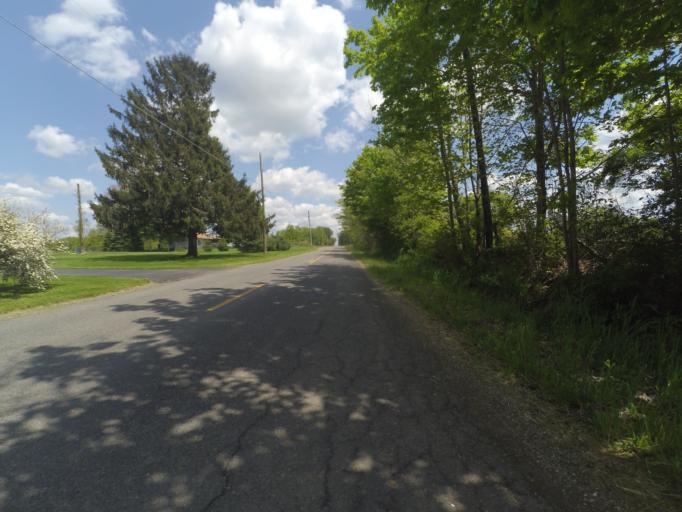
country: US
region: Ohio
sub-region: Portage County
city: Ravenna
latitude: 41.1176
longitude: -81.1282
